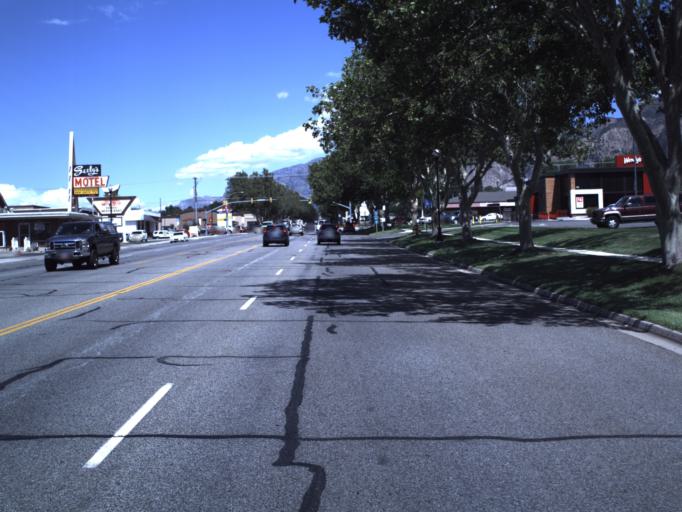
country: US
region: Utah
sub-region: Box Elder County
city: Brigham City
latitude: 41.4943
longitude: -112.0160
